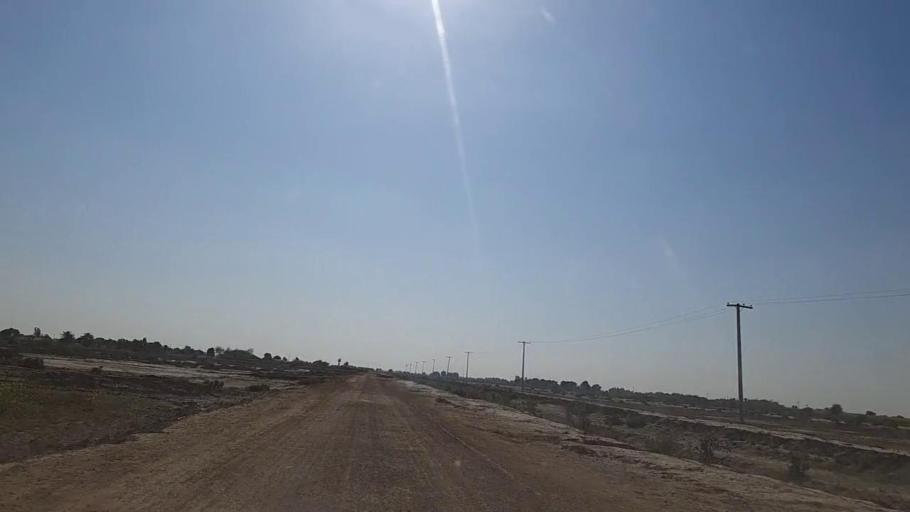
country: PK
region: Sindh
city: Digri
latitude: 25.1288
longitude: 69.0566
